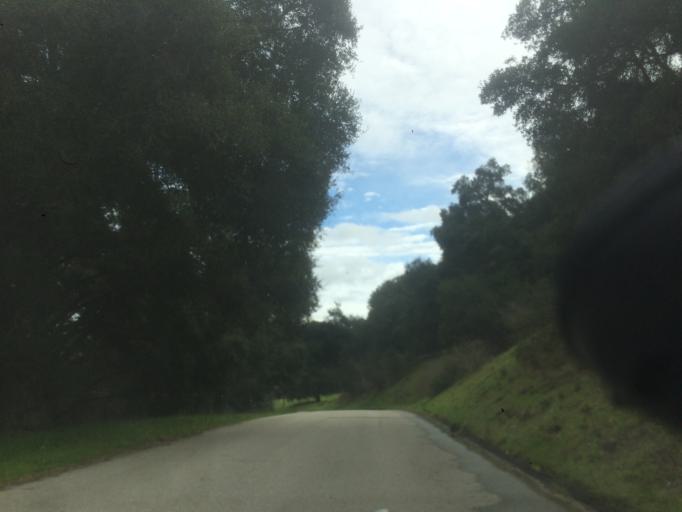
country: US
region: California
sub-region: San Luis Obispo County
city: Nipomo
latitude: 35.2032
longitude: -120.4234
